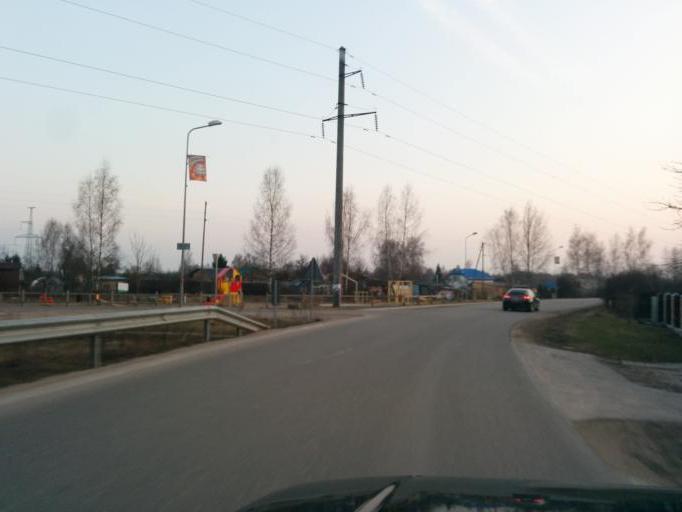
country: LV
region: Kekava
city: Balozi
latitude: 56.8612
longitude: 24.0781
